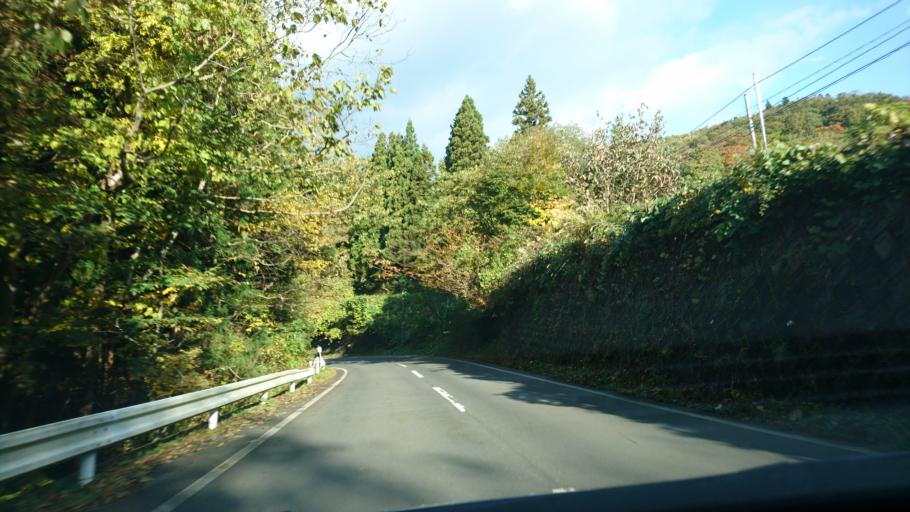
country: JP
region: Iwate
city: Mizusawa
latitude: 39.0660
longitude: 141.0287
